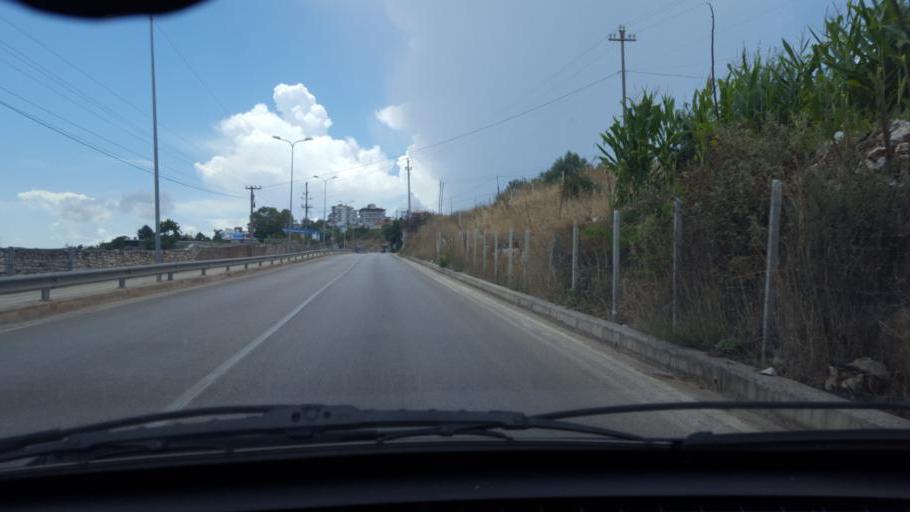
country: AL
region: Vlore
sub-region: Rrethi i Sarandes
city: Sarande
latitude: 39.8464
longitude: 20.0248
